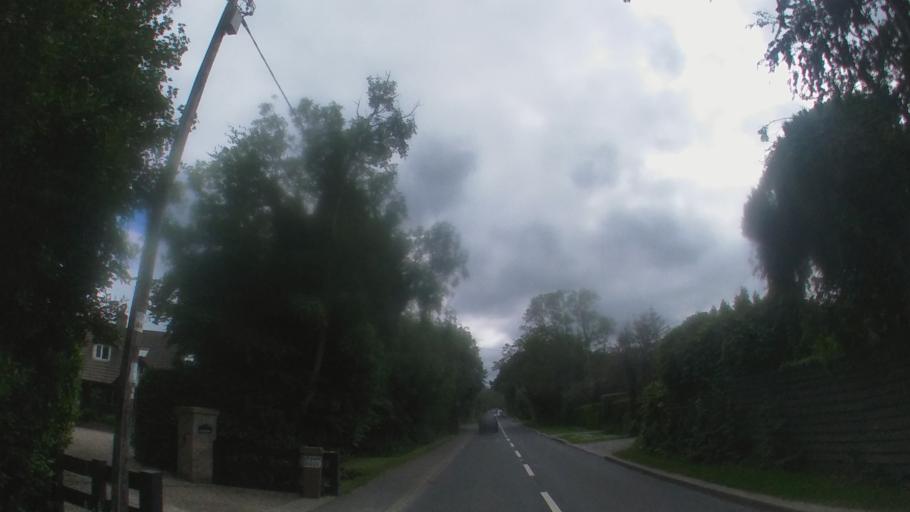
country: IE
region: Leinster
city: Foxrock
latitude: 53.2466
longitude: -6.1843
